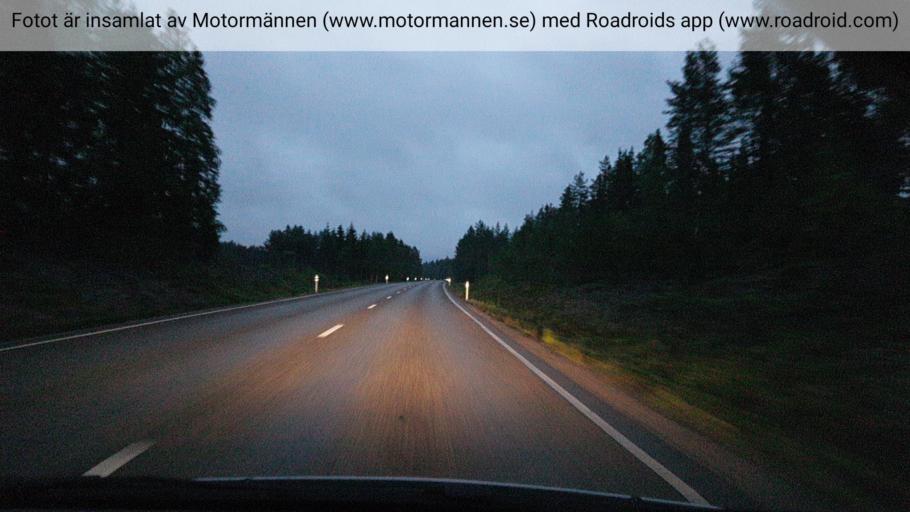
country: SE
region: Vaestmanland
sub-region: Surahammars Kommun
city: Ramnas
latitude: 59.7858
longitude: 16.0162
